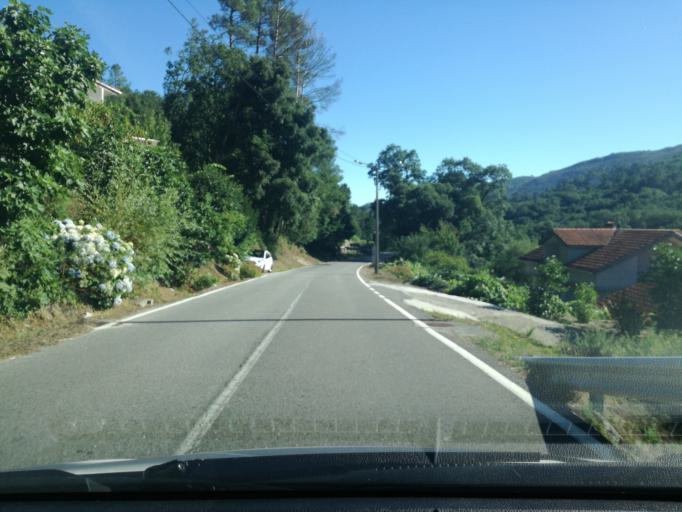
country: ES
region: Galicia
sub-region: Provincia de Ourense
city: Lobios
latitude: 41.8605
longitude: -8.1091
